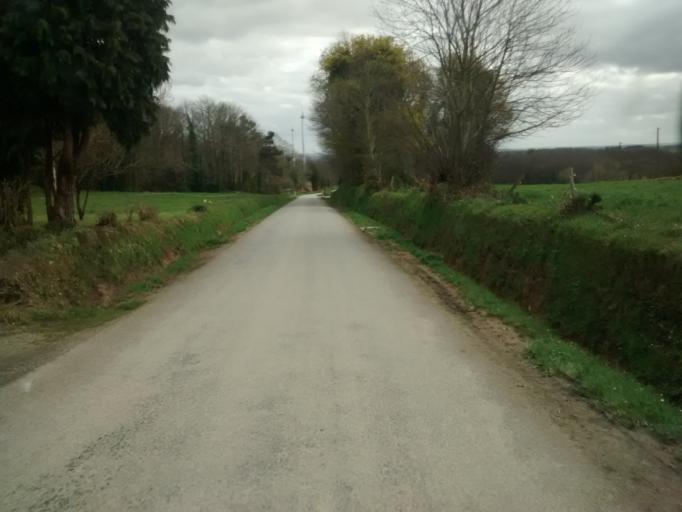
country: FR
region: Brittany
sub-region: Departement du Morbihan
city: Meneac
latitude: 48.1347
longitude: -2.4549
